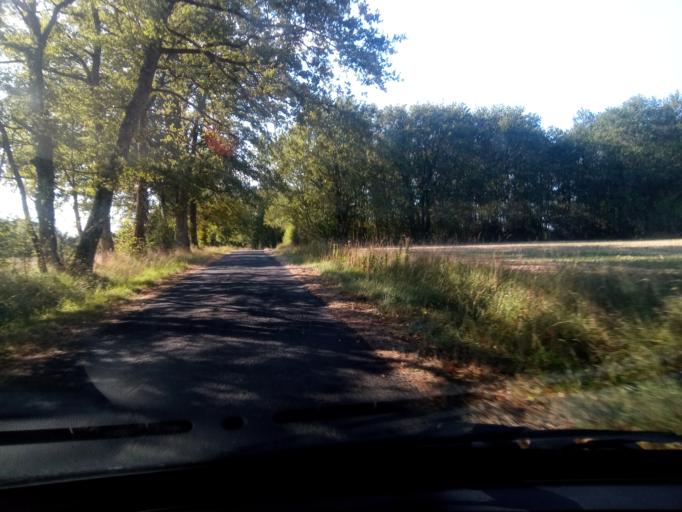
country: FR
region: Poitou-Charentes
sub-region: Departement de la Vienne
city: Montmorillon
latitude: 46.4903
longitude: 0.8028
